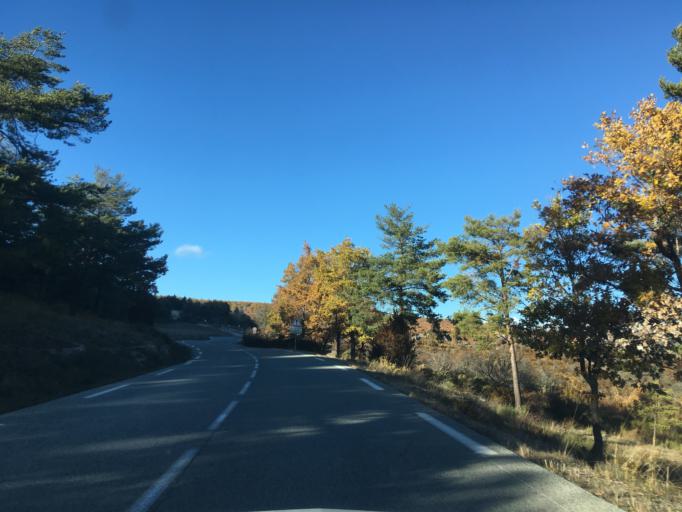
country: FR
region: Provence-Alpes-Cote d'Azur
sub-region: Departement du Var
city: Bargemon
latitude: 43.6931
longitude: 6.5067
